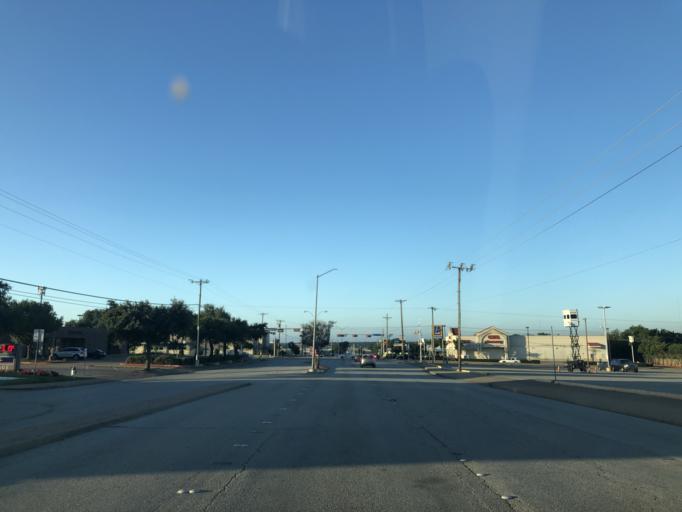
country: US
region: Texas
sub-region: Dallas County
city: Duncanville
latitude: 32.6488
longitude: -96.9256
